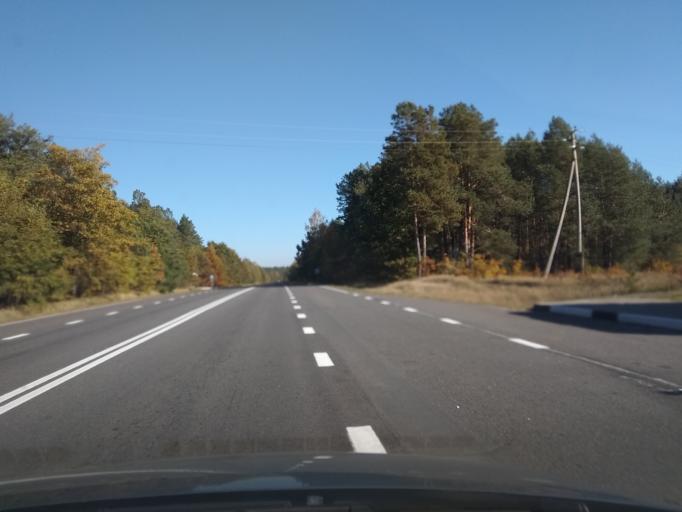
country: BY
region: Brest
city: Kobryn
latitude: 52.0203
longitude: 24.2422
